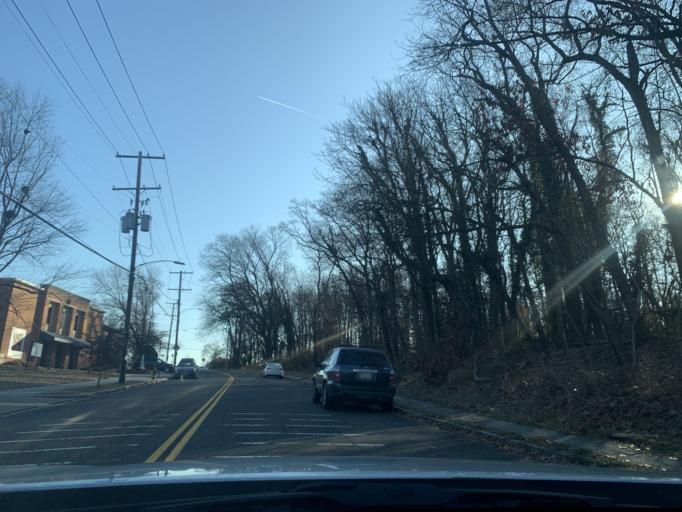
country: US
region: Maryland
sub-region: Prince George's County
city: Coral Hills
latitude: 38.8829
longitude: -76.9485
